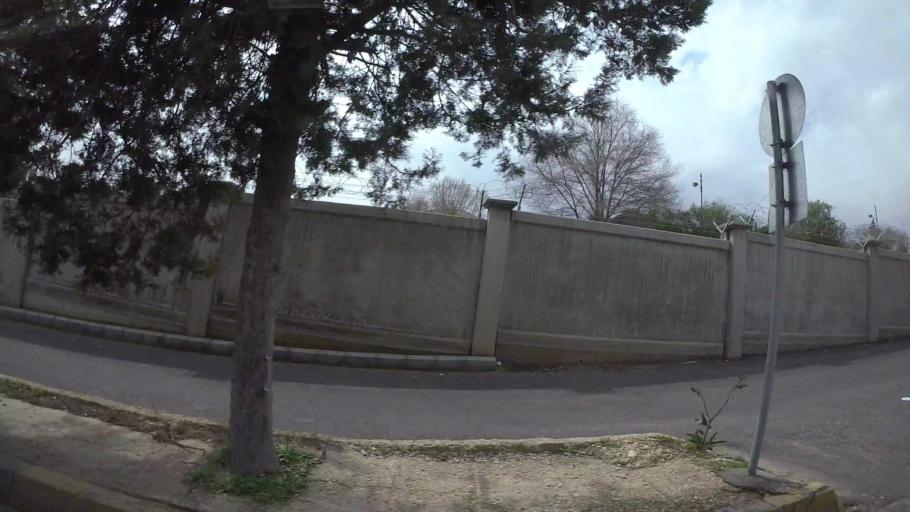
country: JO
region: Amman
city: Amman
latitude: 31.9613
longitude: 35.9498
